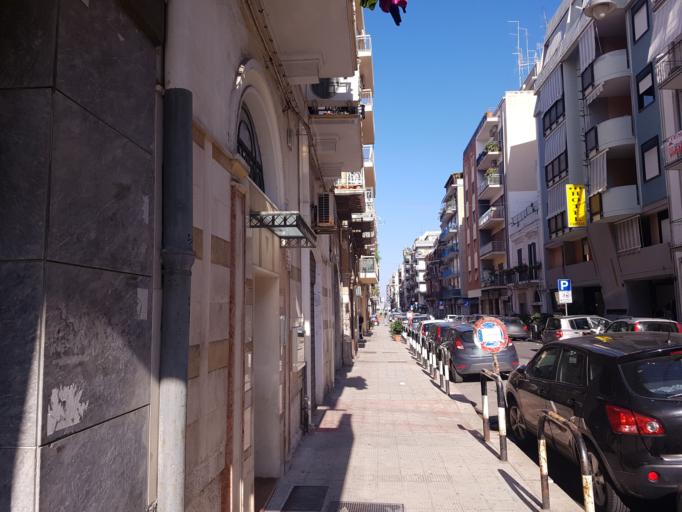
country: IT
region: Apulia
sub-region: Provincia di Bari
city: Bari
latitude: 41.1201
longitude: 16.8602
